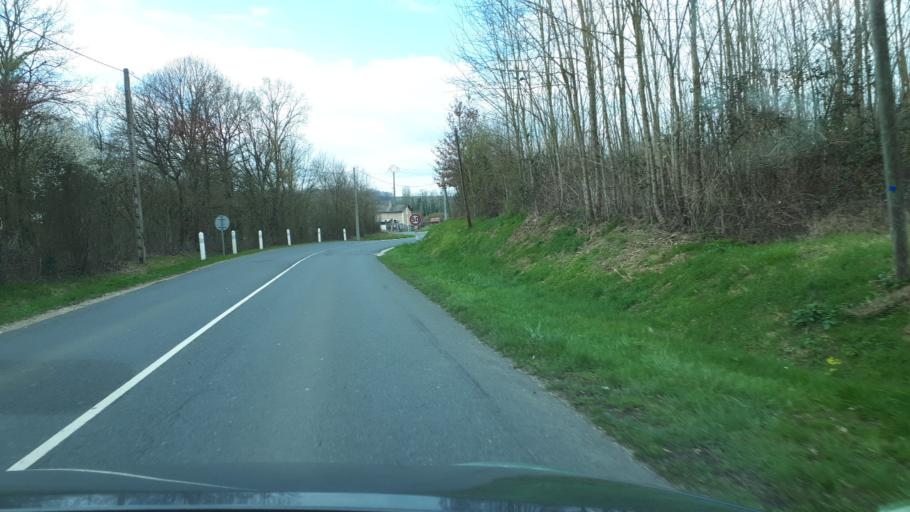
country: FR
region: Centre
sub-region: Departement du Loir-et-Cher
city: Villiers-sur-Loir
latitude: 47.7768
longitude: 0.9898
